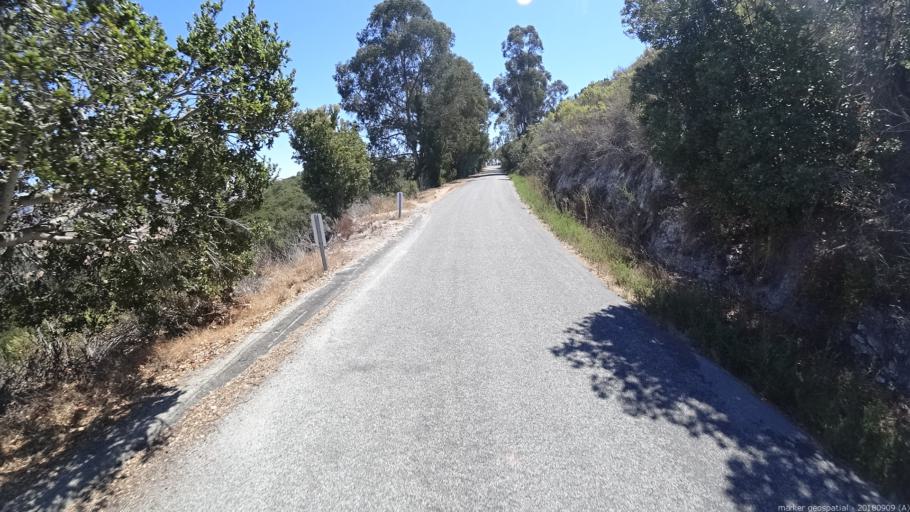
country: US
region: California
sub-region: Monterey County
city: Carmel Valley Village
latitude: 36.5510
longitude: -121.7444
